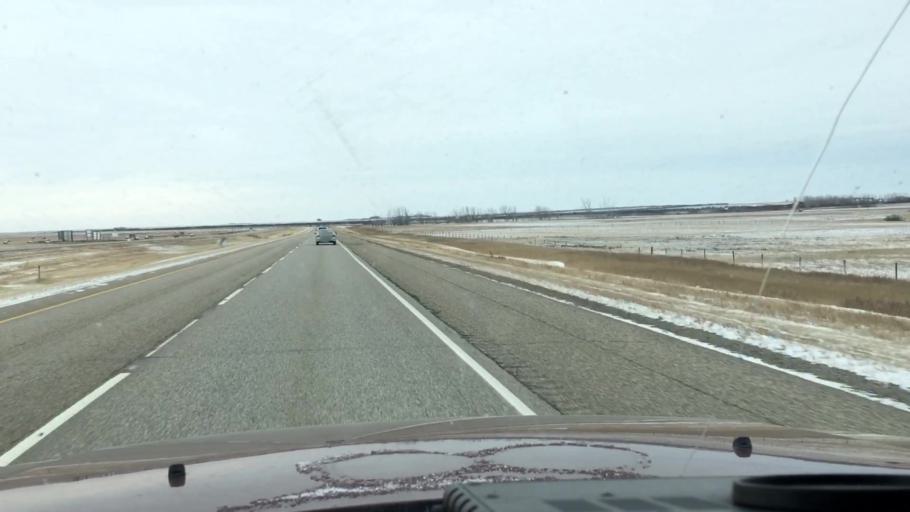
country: CA
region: Saskatchewan
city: Saskatoon
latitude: 51.4835
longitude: -106.2506
